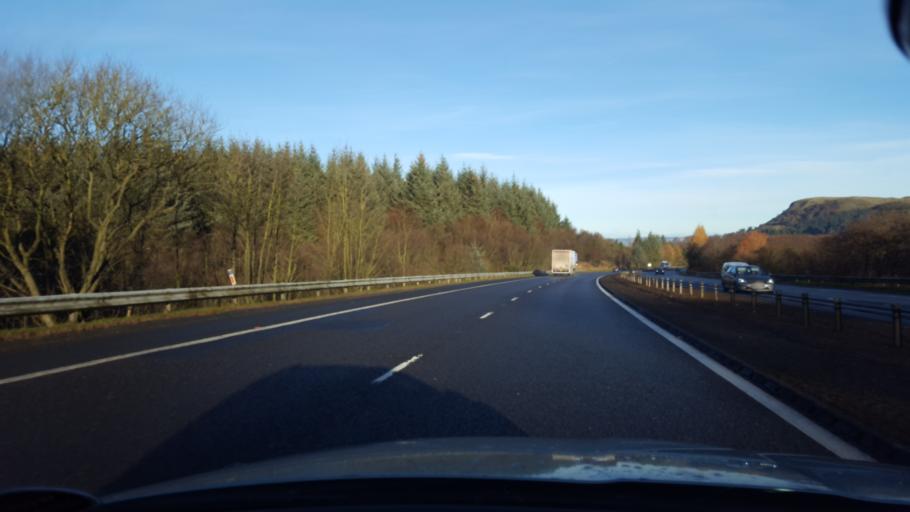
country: GB
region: Scotland
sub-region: Fife
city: Kelty
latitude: 56.1364
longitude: -3.3979
